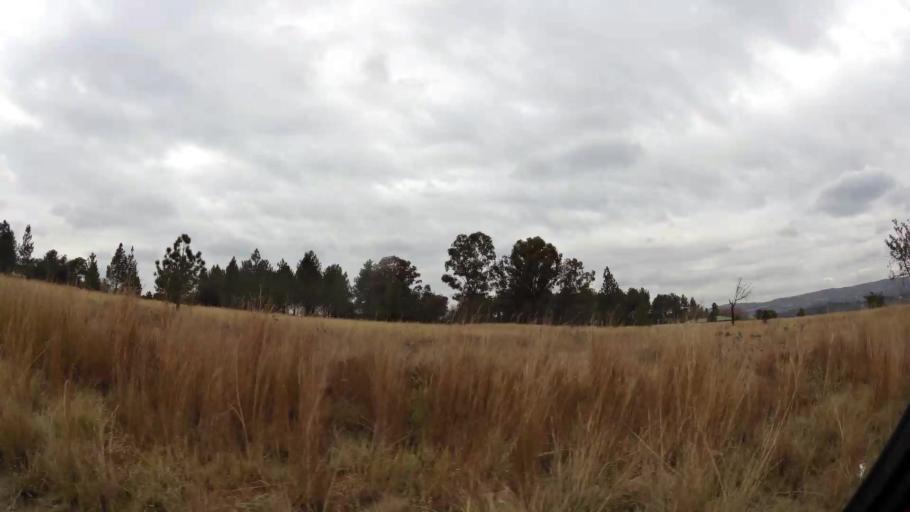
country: ZA
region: Gauteng
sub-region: West Rand District Municipality
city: Muldersdriseloop
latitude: -26.0544
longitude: 27.8888
